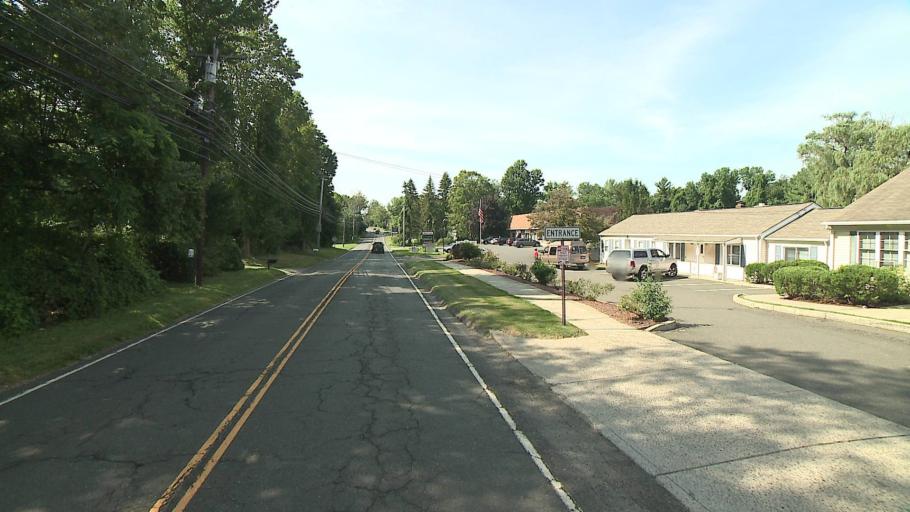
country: US
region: Connecticut
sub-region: Fairfield County
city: Danbury
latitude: 41.4449
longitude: -73.4725
